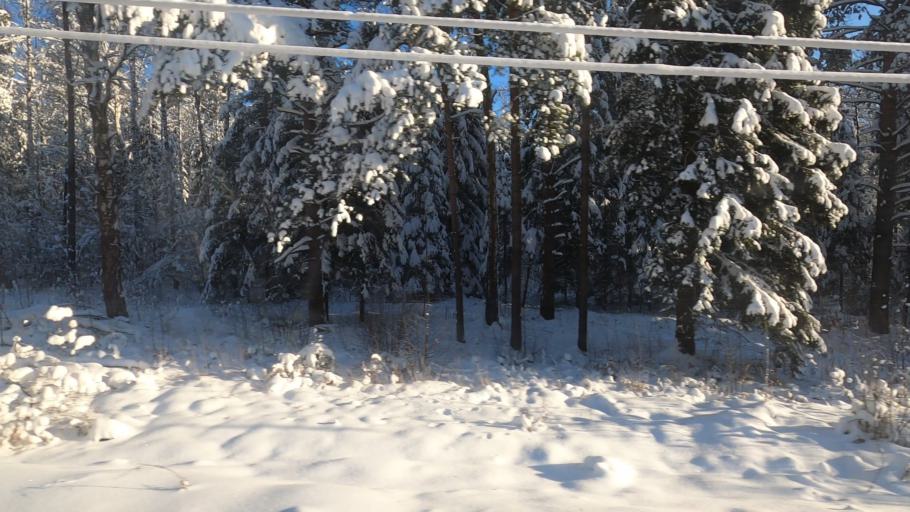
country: RU
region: Moskovskaya
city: Zhukovka
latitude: 56.4850
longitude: 37.5495
